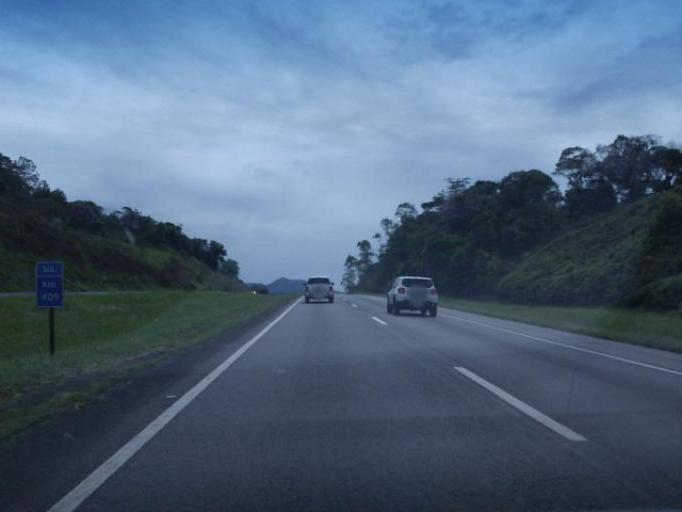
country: BR
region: Sao Paulo
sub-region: Juquia
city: Juquia
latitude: -24.3308
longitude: -47.5834
